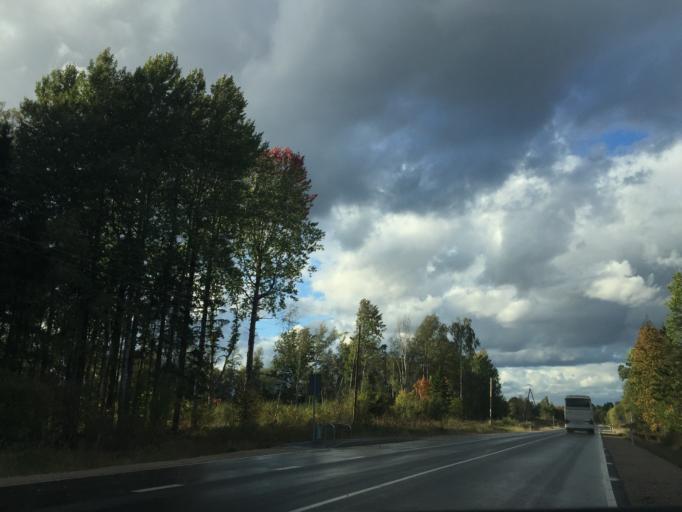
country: LV
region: Ligatne
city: Ligatne
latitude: 57.1388
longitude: 25.0819
